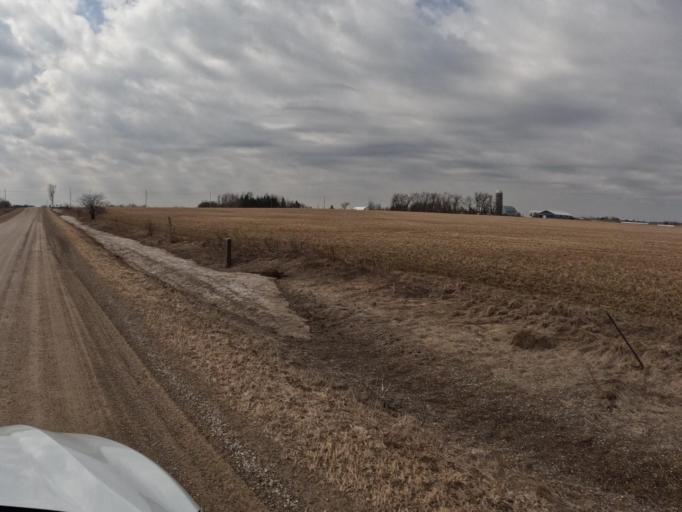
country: CA
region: Ontario
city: Orangeville
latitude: 43.9241
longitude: -80.2188
